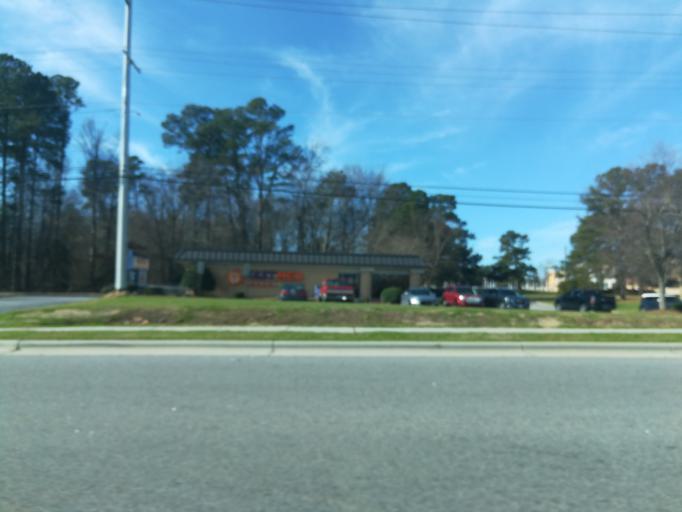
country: US
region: North Carolina
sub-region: Nash County
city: Rocky Mount
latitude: 35.9730
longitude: -77.8488
